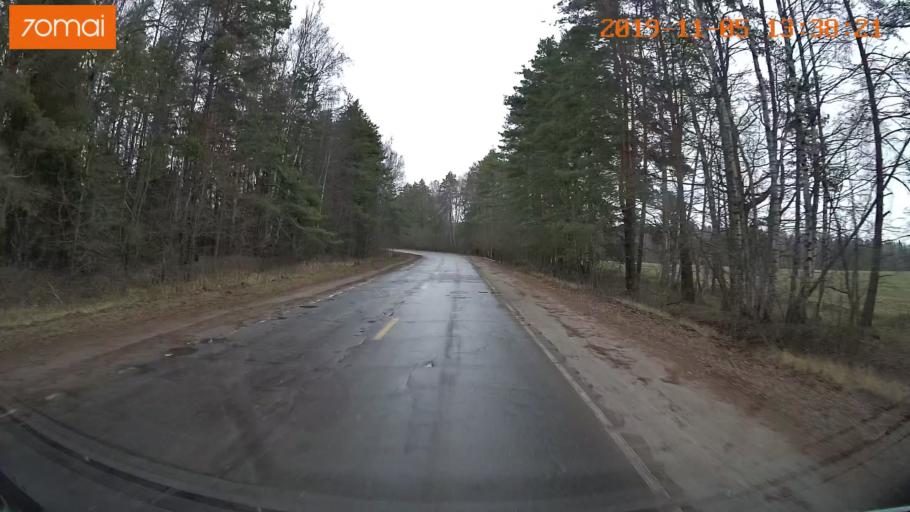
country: RU
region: Ivanovo
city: Shuya
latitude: 56.9310
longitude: 41.3862
